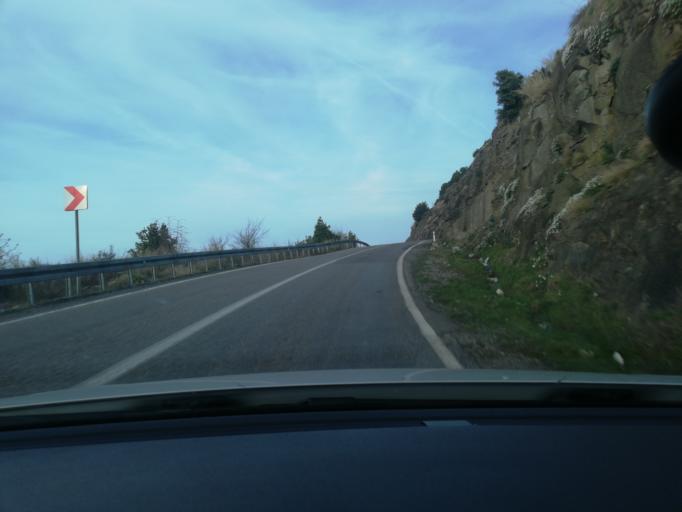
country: TR
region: Zonguldak
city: Tieum
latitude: 41.5500
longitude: 32.0038
